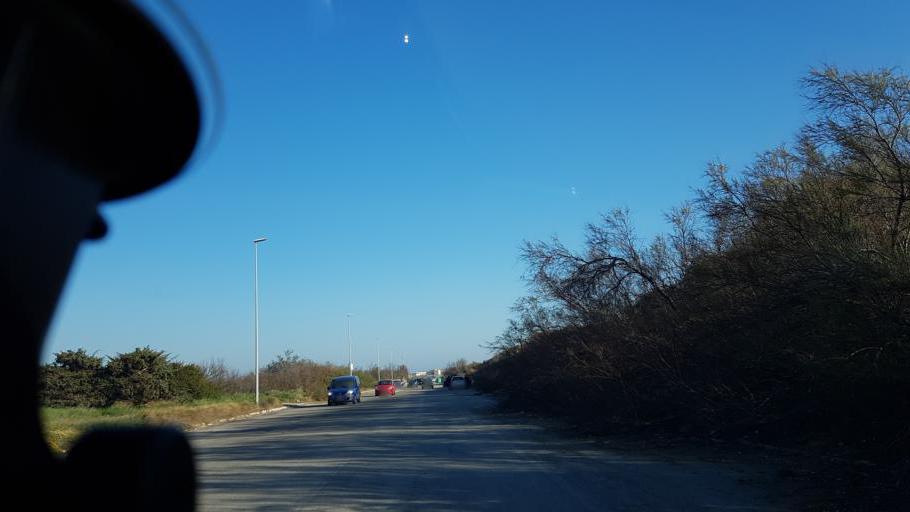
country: IT
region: Apulia
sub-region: Provincia di Lecce
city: Struda
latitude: 40.3949
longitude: 18.2998
